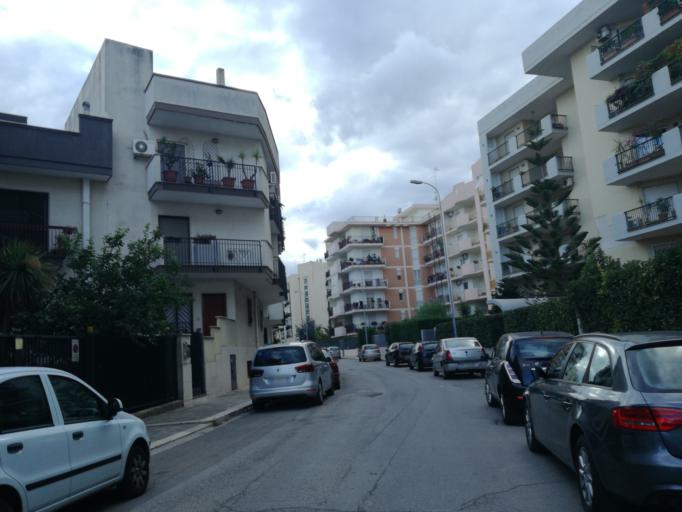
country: IT
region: Apulia
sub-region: Provincia di Bari
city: Triggiano
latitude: 41.0716
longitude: 16.9340
